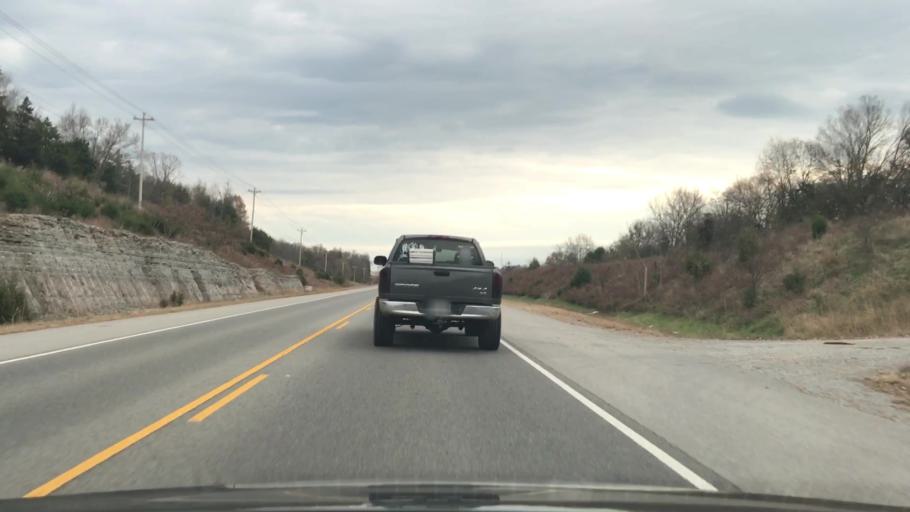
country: US
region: Tennessee
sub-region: Wilson County
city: Lebanon
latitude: 36.2705
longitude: -86.2330
